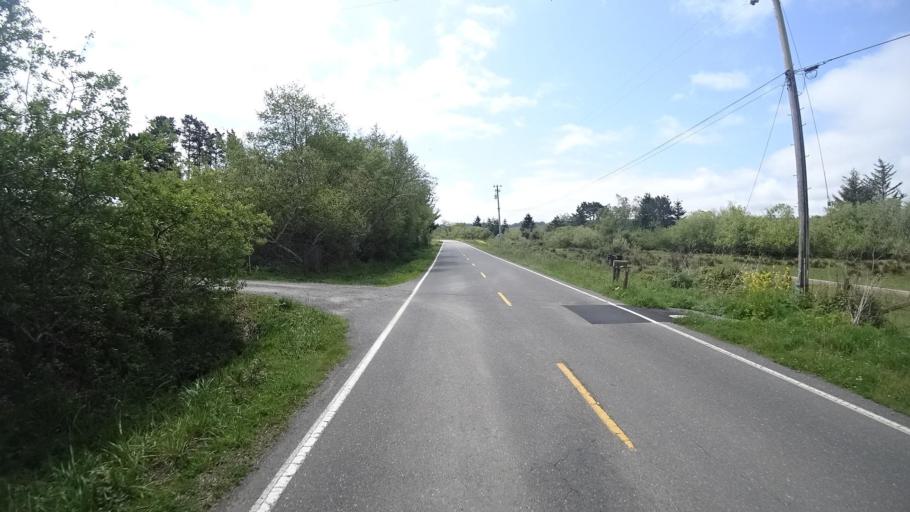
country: US
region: California
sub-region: Humboldt County
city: Humboldt Hill
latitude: 40.6828
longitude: -124.1993
